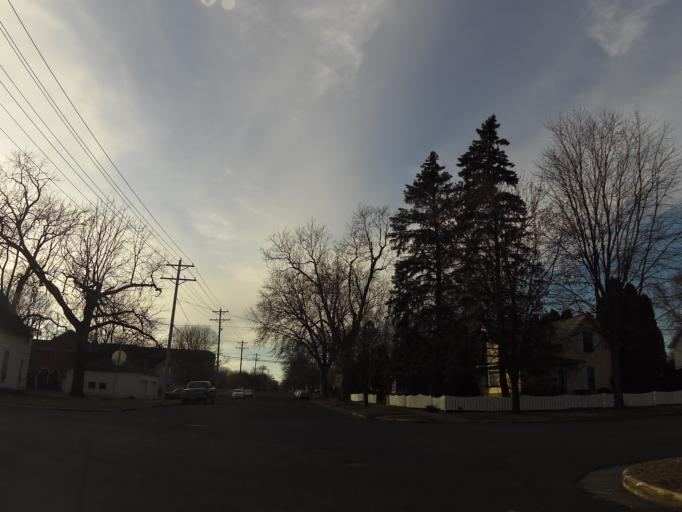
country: US
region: Wisconsin
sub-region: Pierce County
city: River Falls
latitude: 44.8607
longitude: -92.6279
